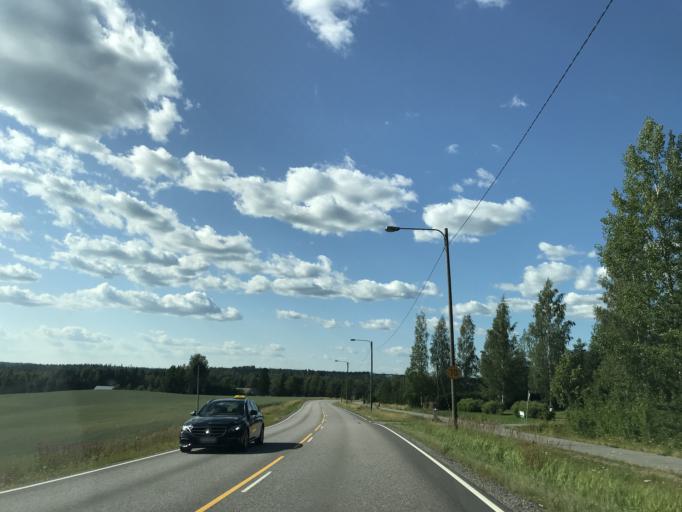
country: FI
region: Uusimaa
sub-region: Helsinki
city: Nurmijaervi
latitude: 60.4276
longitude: 24.8584
